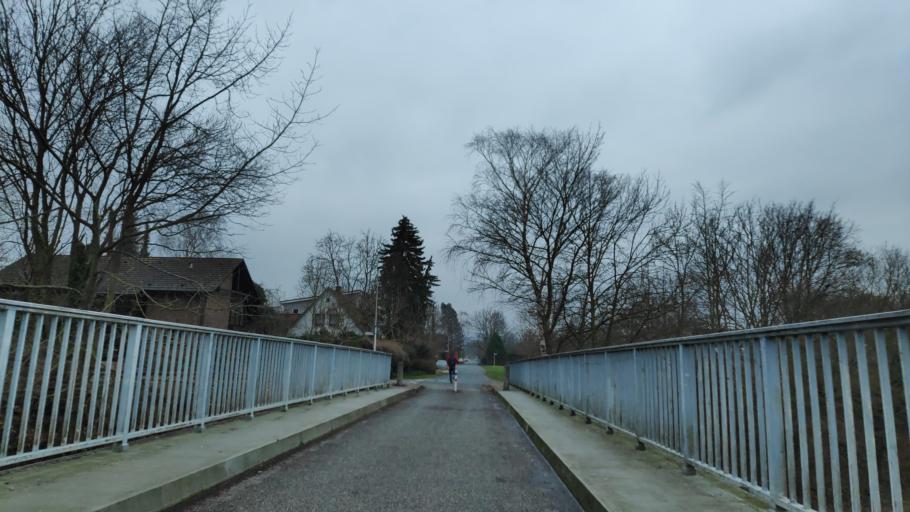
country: DE
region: North Rhine-Westphalia
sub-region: Regierungsbezirk Detmold
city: Minden
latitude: 52.3008
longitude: 8.8879
